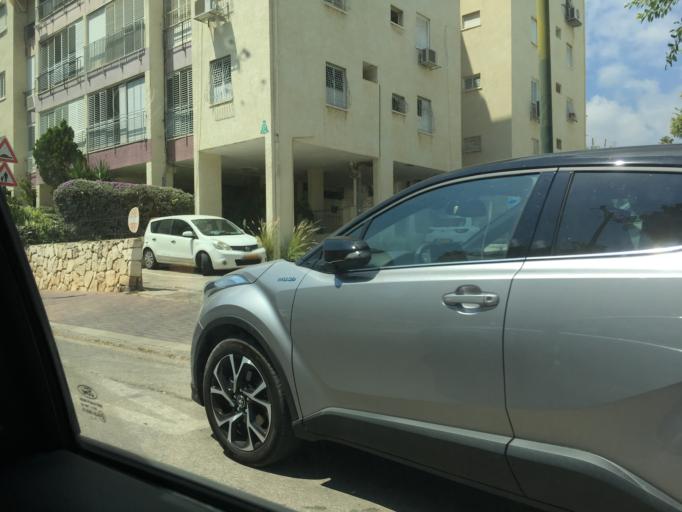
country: IL
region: Tel Aviv
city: Ramat HaSharon
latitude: 32.1397
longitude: 34.8413
